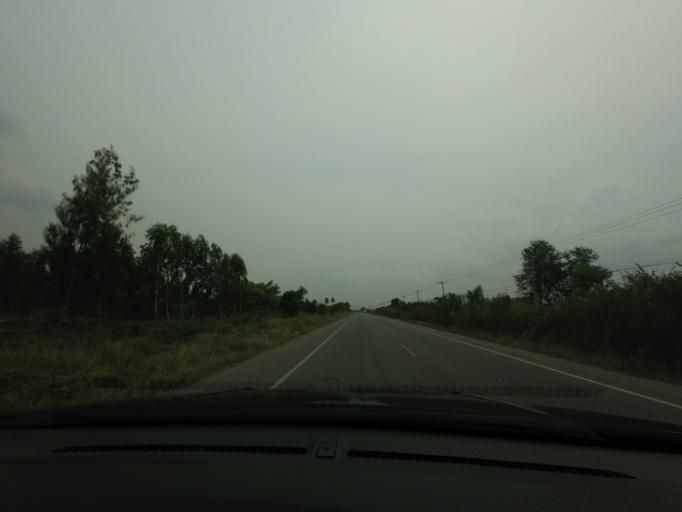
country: TH
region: Phetchaburi
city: Ban Laem
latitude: 13.1732
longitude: 99.9280
